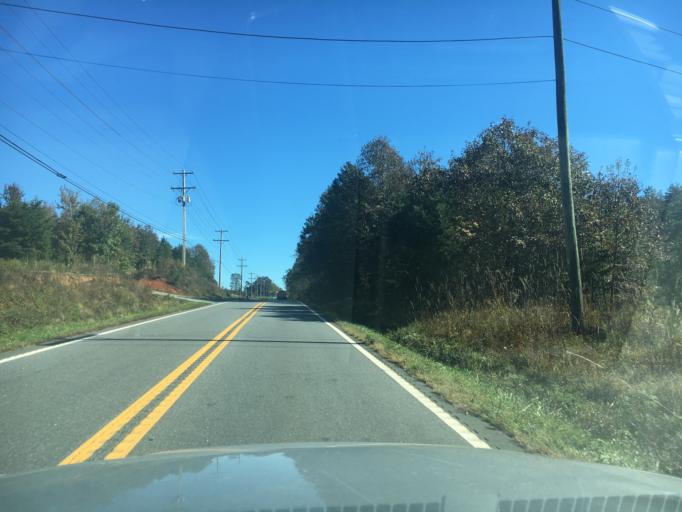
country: US
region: North Carolina
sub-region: Rutherford County
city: Spindale
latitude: 35.4127
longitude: -81.9181
